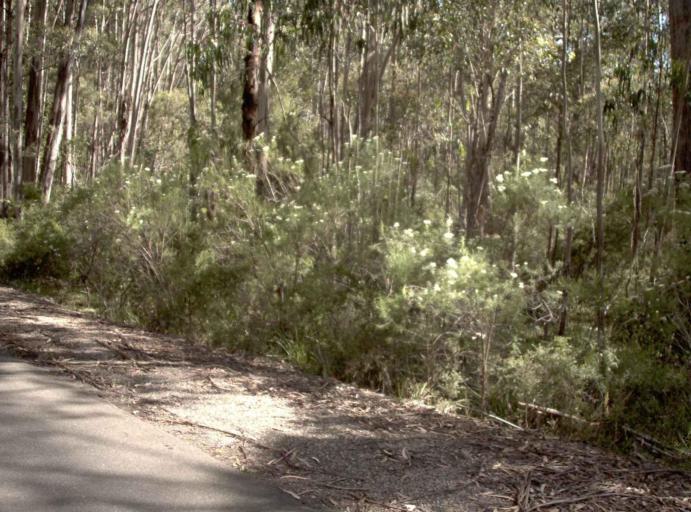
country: AU
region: Victoria
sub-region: East Gippsland
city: Lakes Entrance
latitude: -37.4282
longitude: 148.1270
